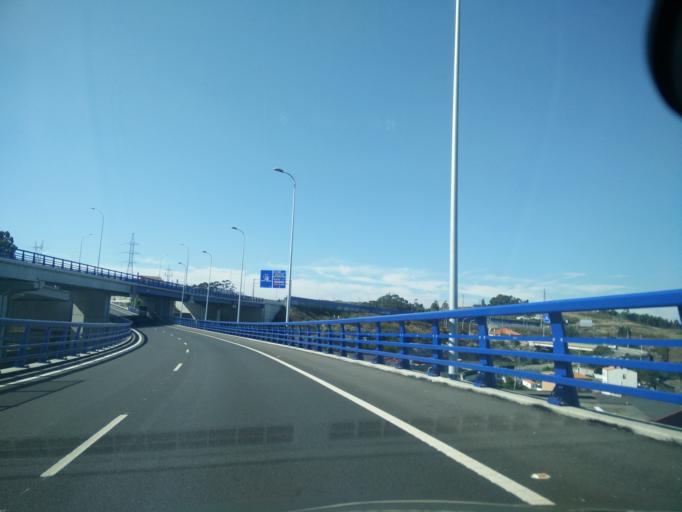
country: ES
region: Galicia
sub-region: Provincia da Coruna
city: A Coruna
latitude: 43.3371
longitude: -8.4212
